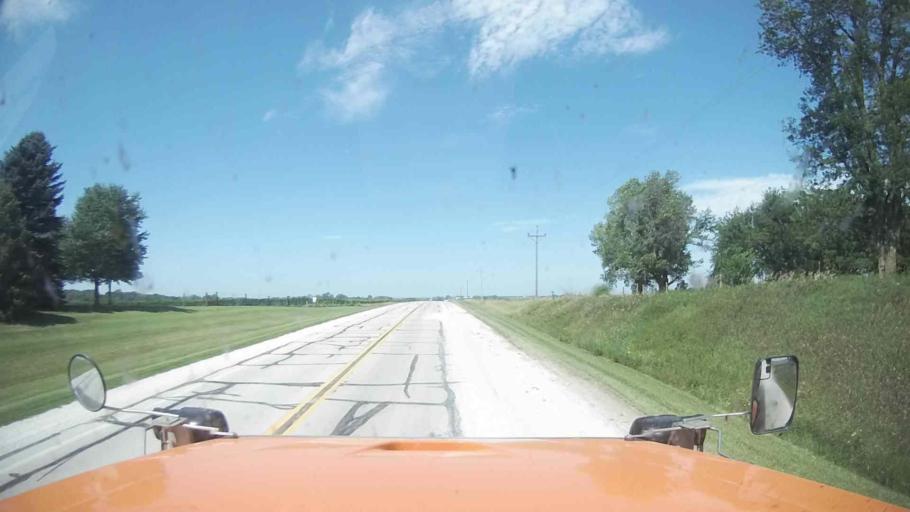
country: US
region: Iowa
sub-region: Calhoun County
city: Lake City
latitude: 42.2604
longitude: -94.8163
